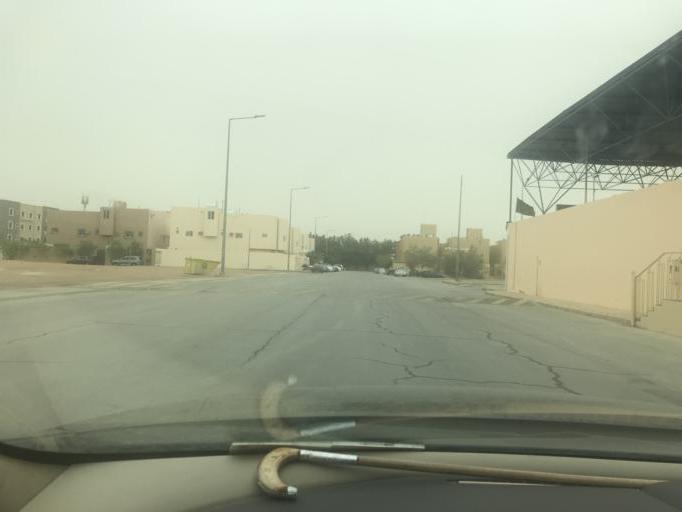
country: SA
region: Ar Riyad
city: Riyadh
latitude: 24.7287
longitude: 46.7899
